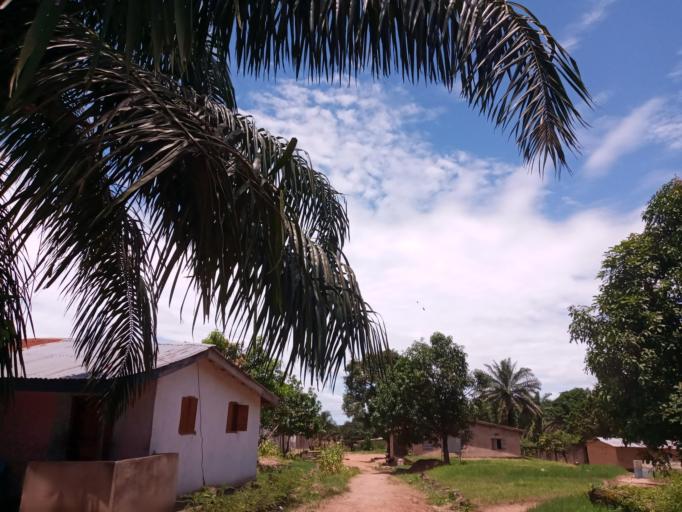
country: SL
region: Eastern Province
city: Koidu
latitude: 8.6491
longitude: -10.9594
